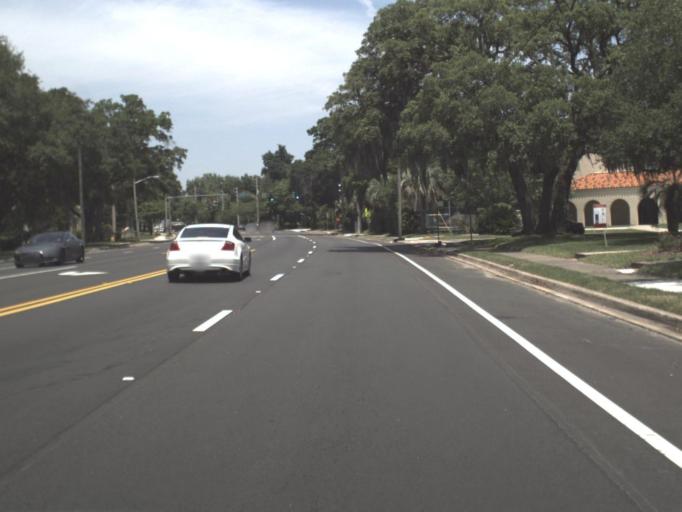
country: US
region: Florida
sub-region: Duval County
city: Jacksonville
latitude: 30.2434
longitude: -81.6265
